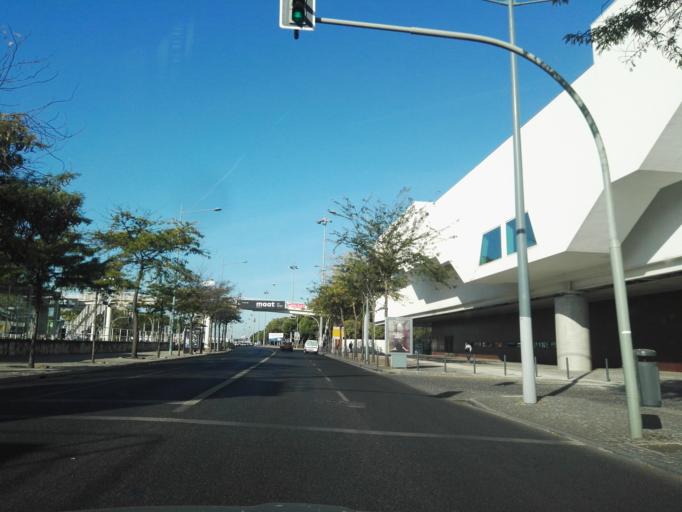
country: PT
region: Setubal
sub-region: Almada
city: Caparica
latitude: 38.6964
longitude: -9.1978
